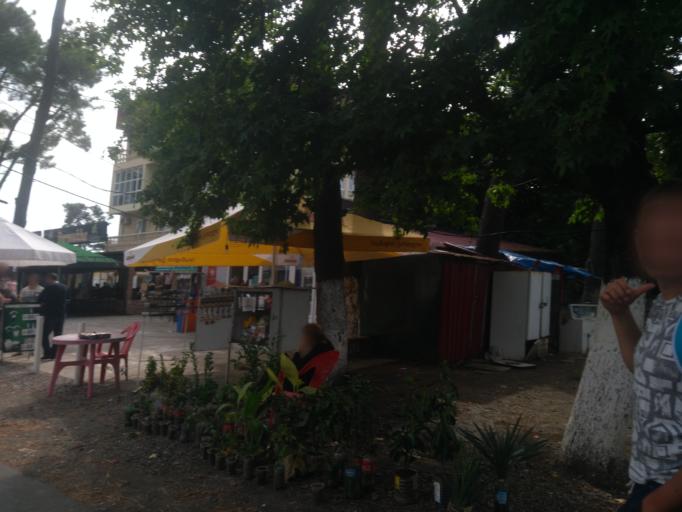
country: GE
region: Guria
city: Urek'i
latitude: 41.9972
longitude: 41.7600
